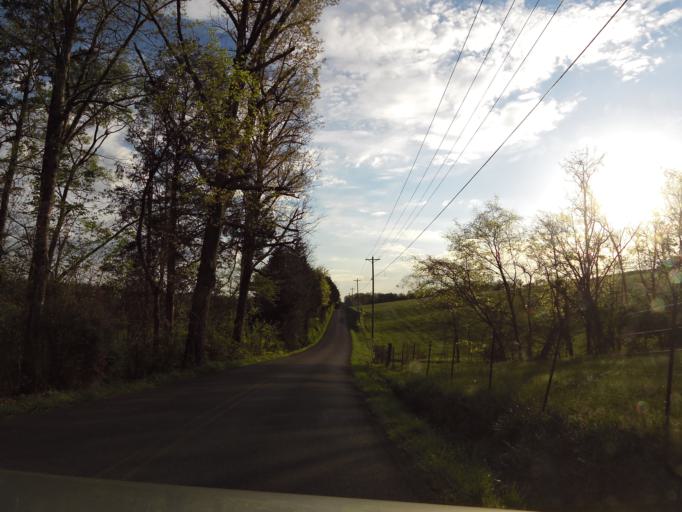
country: US
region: Tennessee
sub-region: Loudon County
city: Greenback
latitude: 35.6401
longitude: -84.0413
